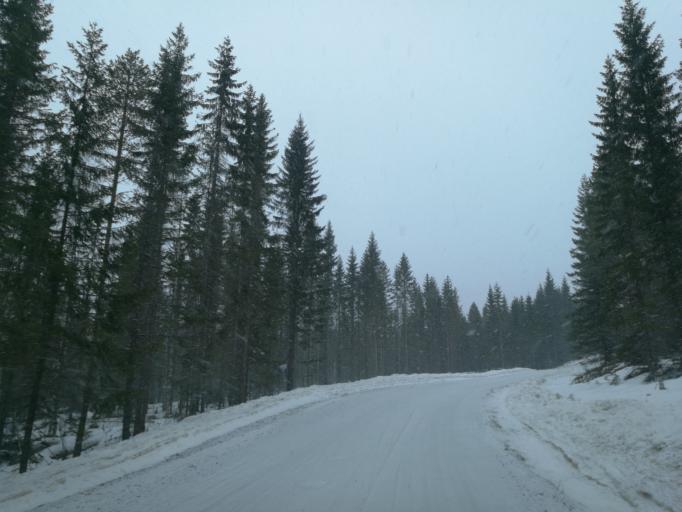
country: SE
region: Vaermland
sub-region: Torsby Kommun
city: Torsby
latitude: 60.6549
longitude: 12.8020
